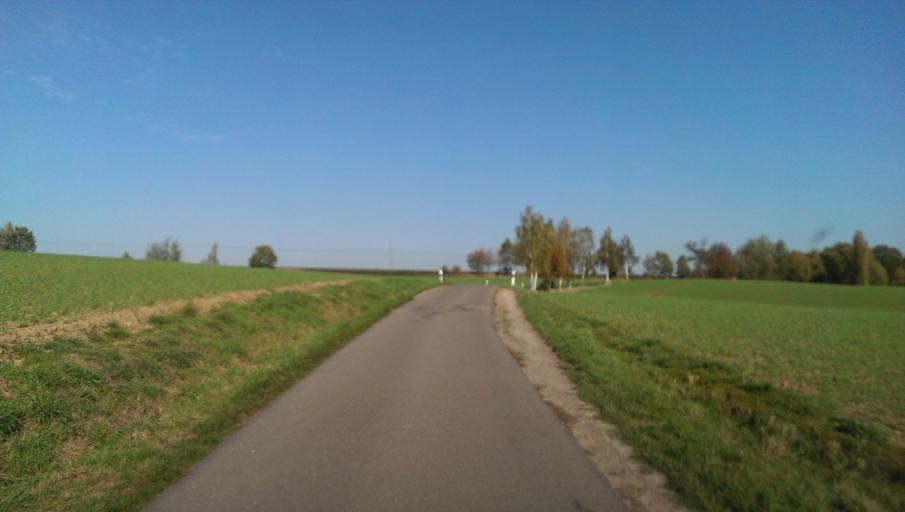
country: DE
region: Saxony
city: Kriebstein
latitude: 51.0504
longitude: 12.9872
